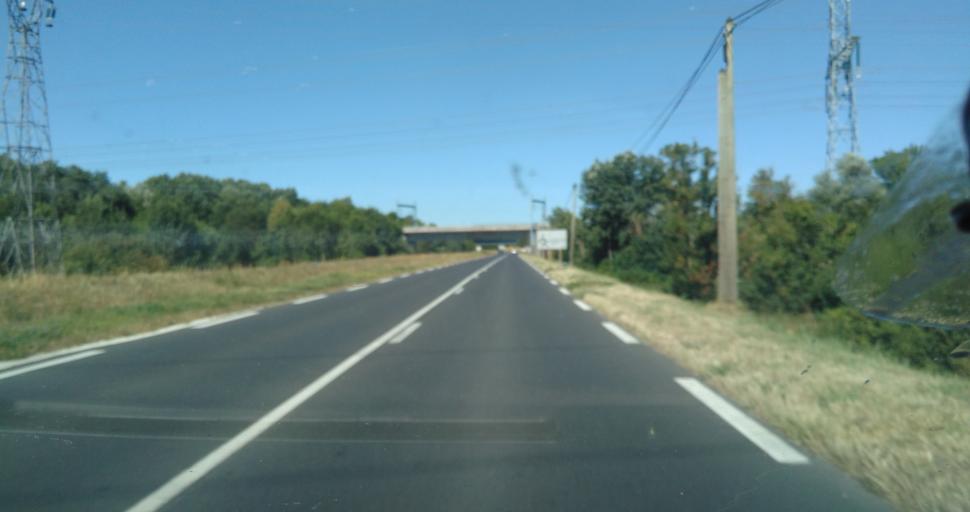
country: FR
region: Centre
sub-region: Departement d'Indre-et-Loire
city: Vouvray
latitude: 47.4019
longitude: 0.8119
